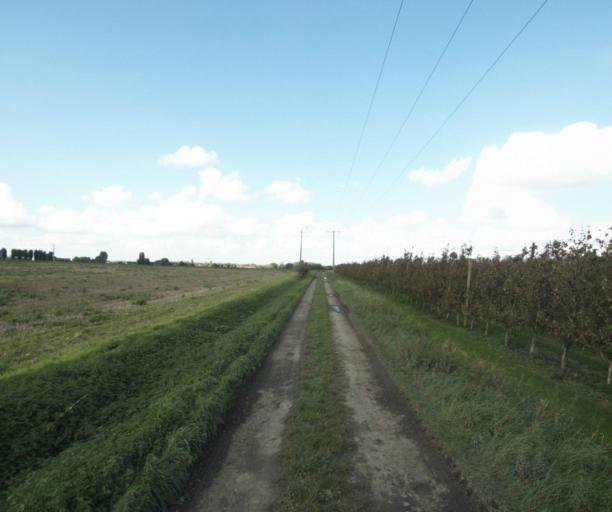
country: FR
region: Nord-Pas-de-Calais
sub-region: Departement du Nord
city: Aubers
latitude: 50.5833
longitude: 2.8255
